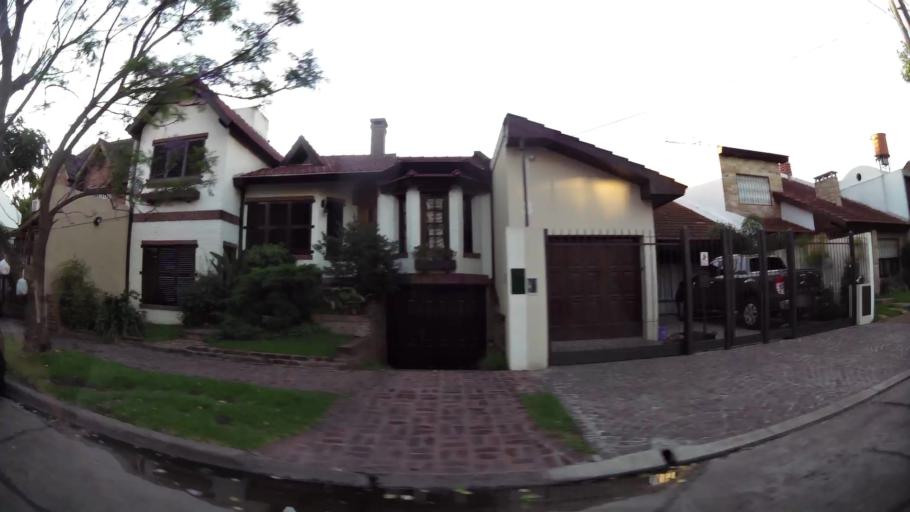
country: AR
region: Buenos Aires
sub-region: Partido de Moron
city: Moron
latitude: -34.6488
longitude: -58.6374
